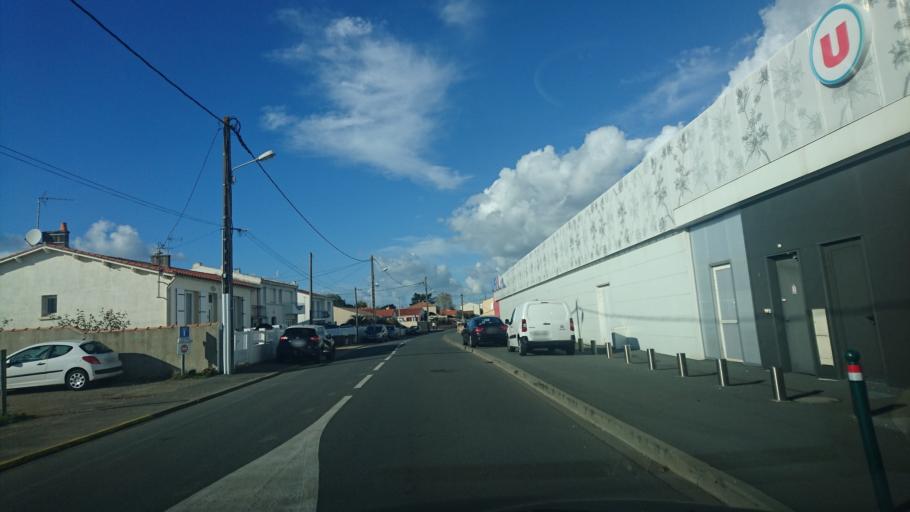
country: FR
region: Pays de la Loire
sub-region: Departement de la Vendee
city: Les Sables-d'Olonne
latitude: 46.5035
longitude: -1.7994
